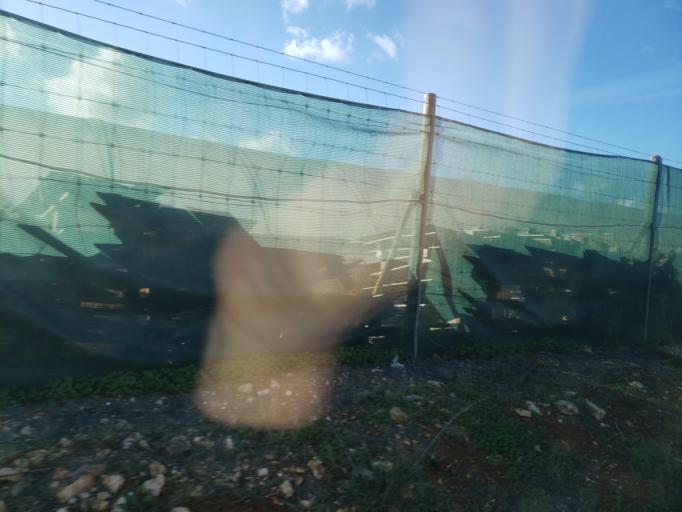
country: PT
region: Faro
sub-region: Portimao
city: Alvor
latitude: 37.1922
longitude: -8.5894
